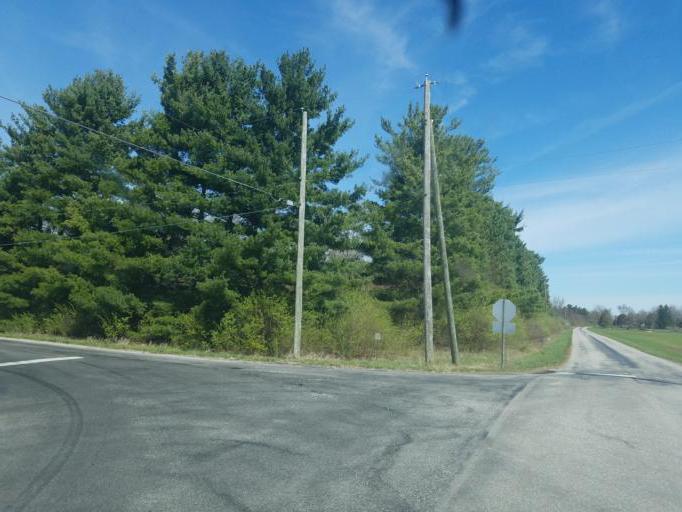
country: US
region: Ohio
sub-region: Delaware County
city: Delaware
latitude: 40.3533
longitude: -83.0548
